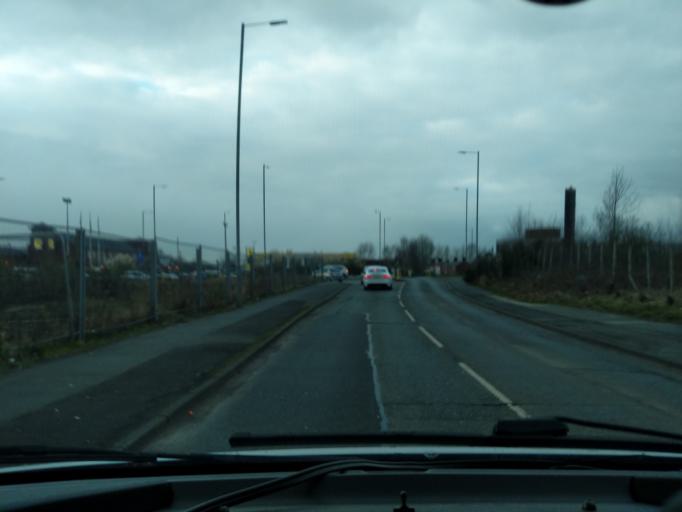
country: GB
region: England
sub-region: St. Helens
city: St Helens
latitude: 53.4419
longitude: -2.7104
